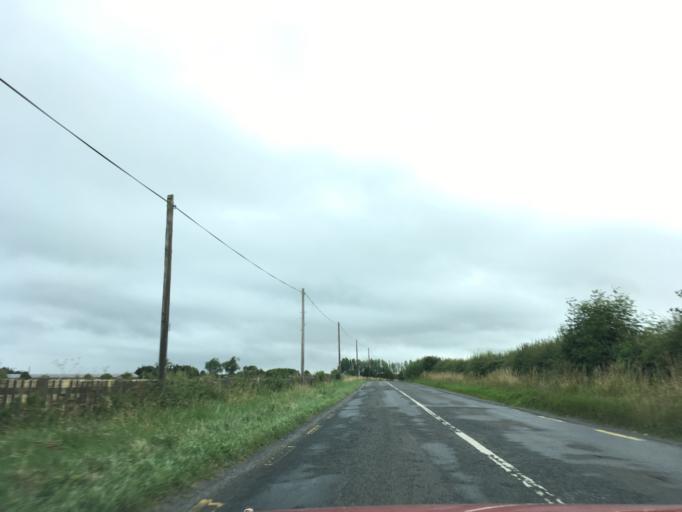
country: IE
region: Munster
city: Cashel
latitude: 52.4478
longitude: -7.8085
